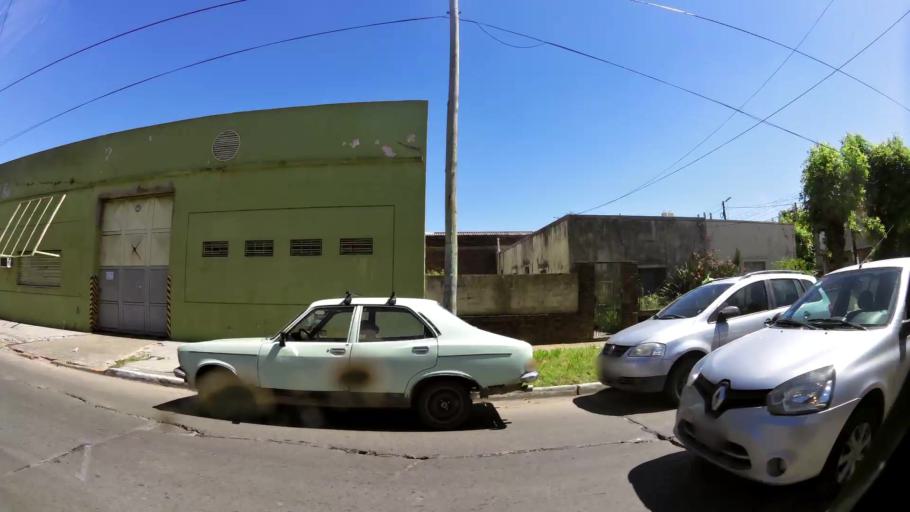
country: AR
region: Buenos Aires
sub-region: Partido de Quilmes
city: Quilmes
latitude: -34.7194
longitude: -58.2807
